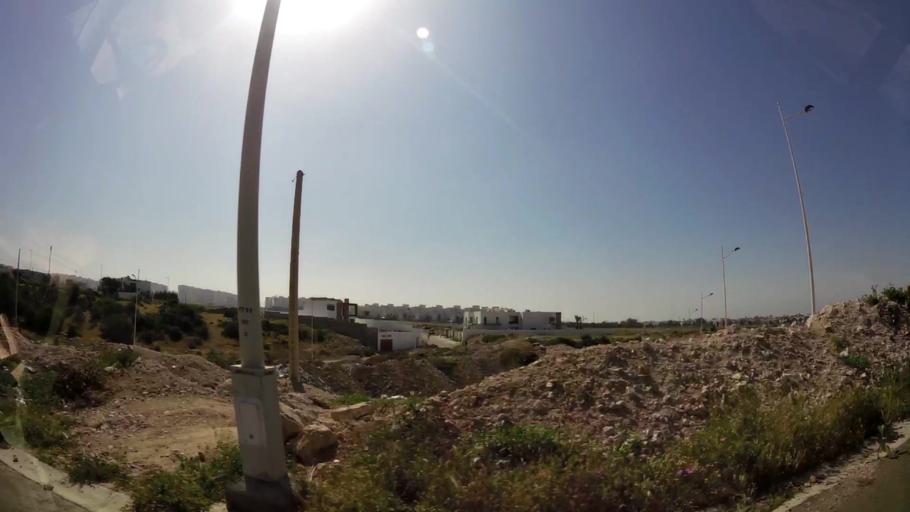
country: MA
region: Souss-Massa-Draa
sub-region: Agadir-Ida-ou-Tnan
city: Agadir
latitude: 30.4391
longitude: -9.5777
